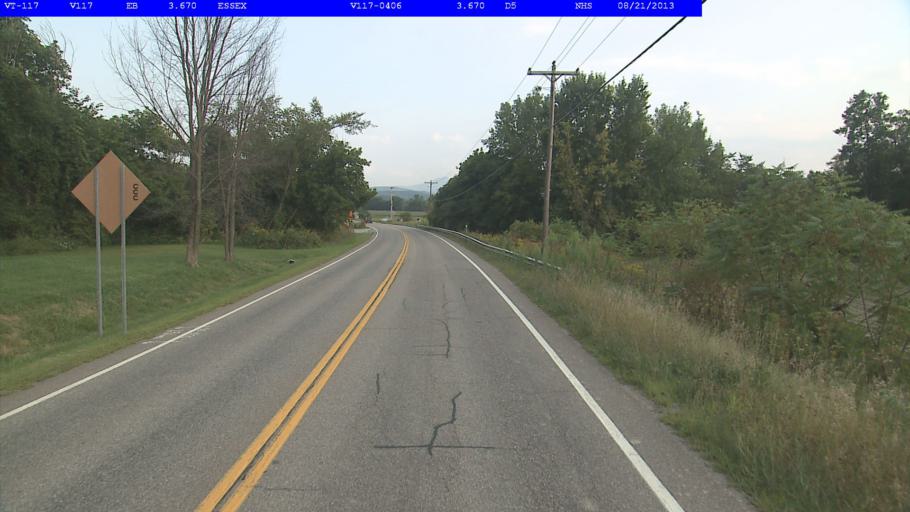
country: US
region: Vermont
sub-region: Chittenden County
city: Williston
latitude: 44.4766
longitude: -73.0430
